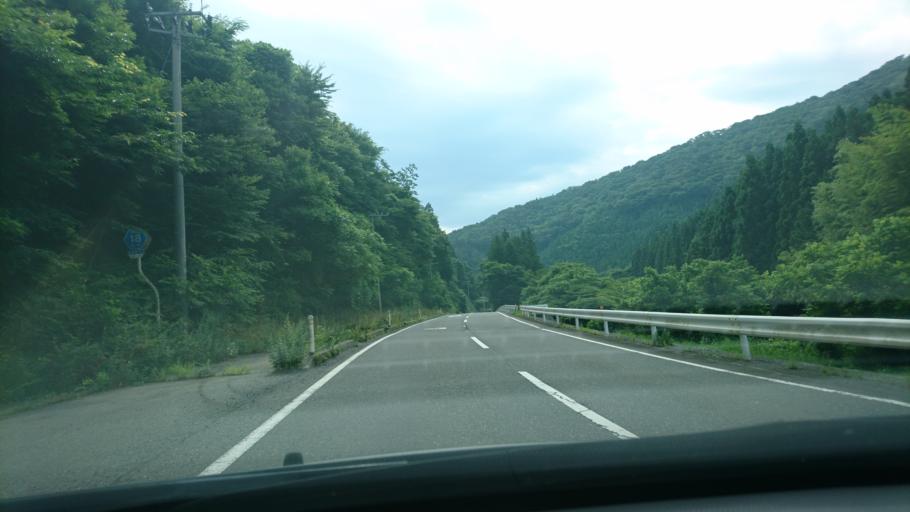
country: JP
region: Iwate
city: Ichinoseki
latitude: 38.8216
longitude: 141.4546
